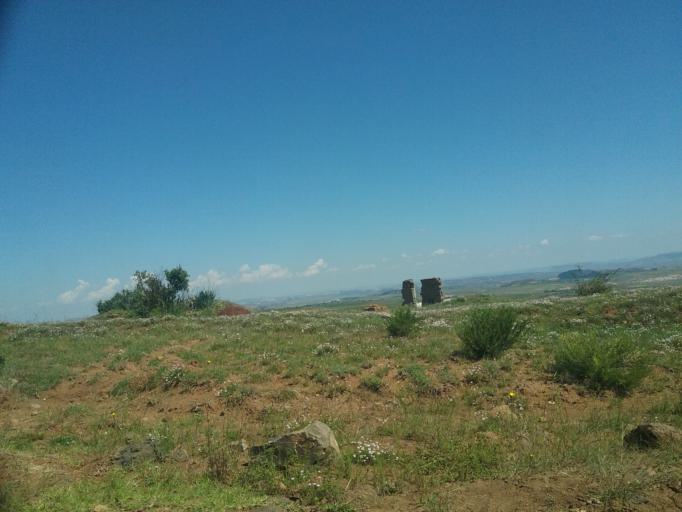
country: LS
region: Berea
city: Teyateyaneng
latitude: -29.2166
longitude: 27.8676
